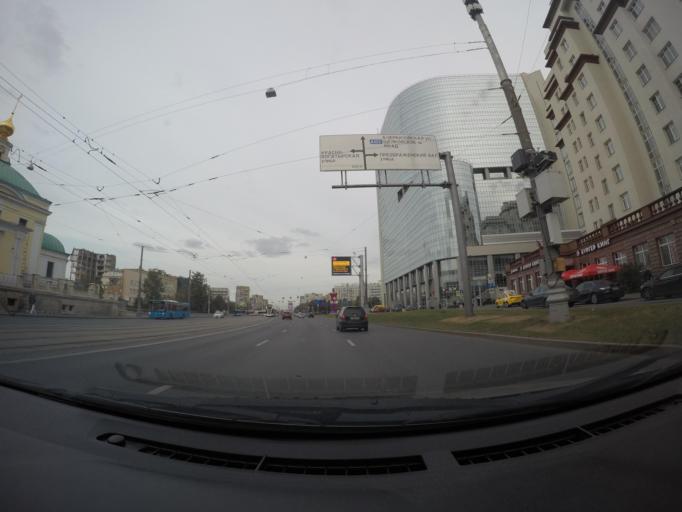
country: RU
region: Moskovskaya
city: Bogorodskoye
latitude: 55.7952
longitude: 37.7110
